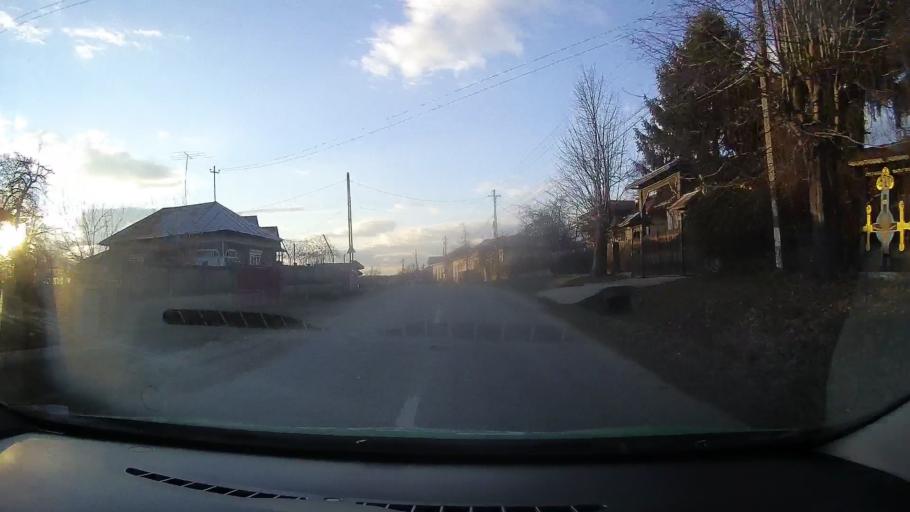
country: RO
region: Dambovita
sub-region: Comuna Gura Ocnitei
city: Adanca
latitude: 44.9201
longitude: 25.6151
